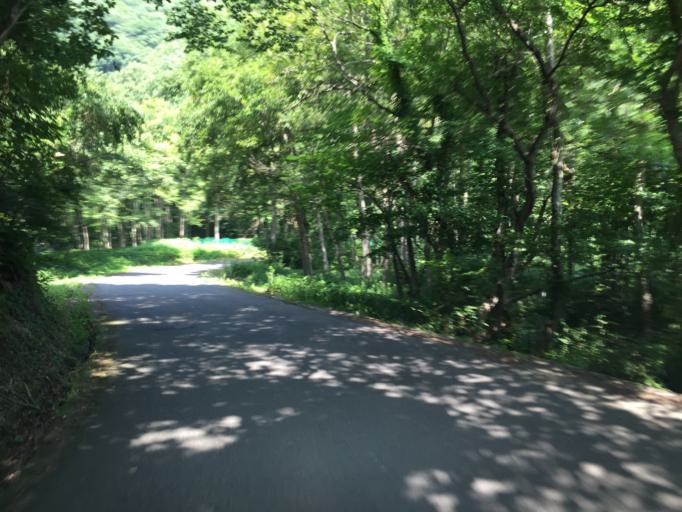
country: JP
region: Fukushima
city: Inawashiro
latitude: 37.4173
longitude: 140.0963
